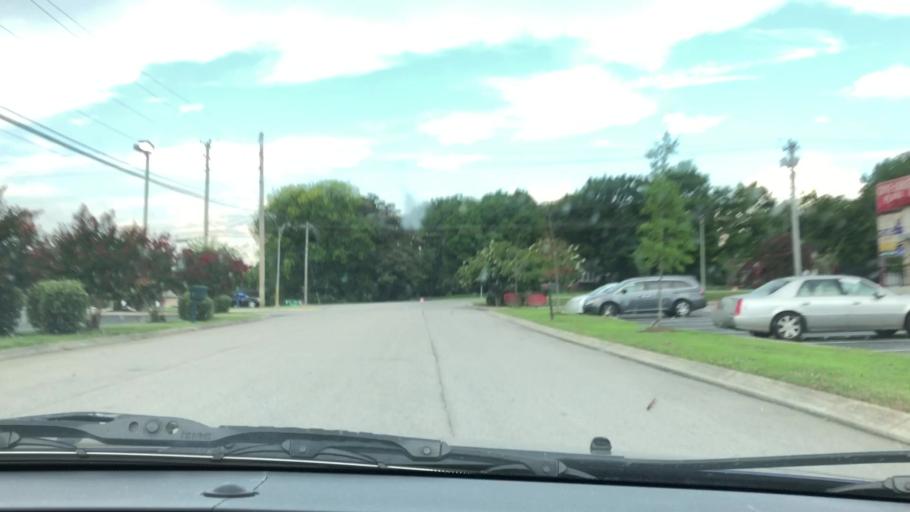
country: US
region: Tennessee
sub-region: Maury County
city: Columbia
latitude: 35.6392
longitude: -87.0144
